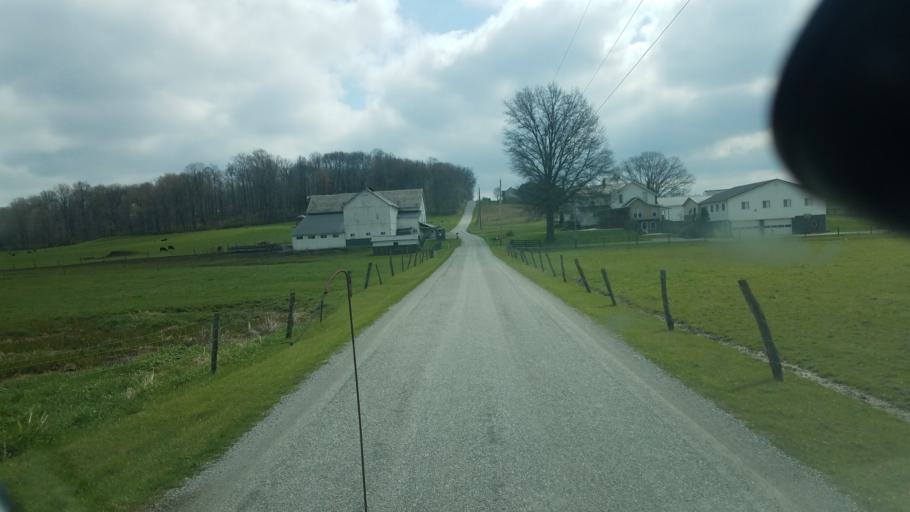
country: US
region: Ohio
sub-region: Holmes County
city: Millersburg
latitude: 40.6131
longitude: -81.8164
